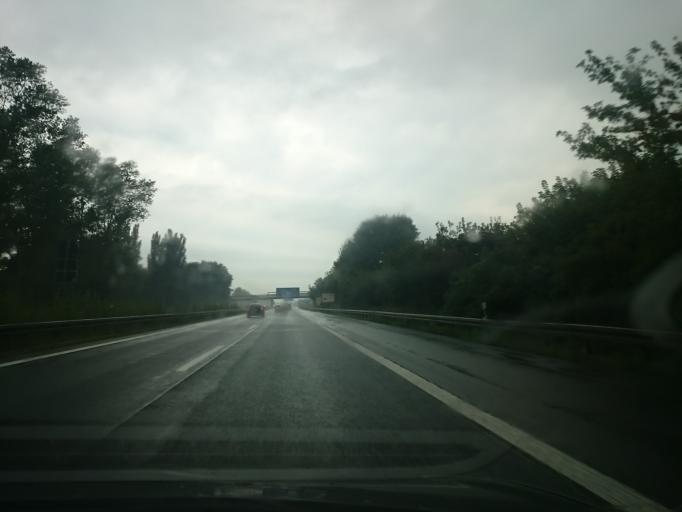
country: DE
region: Brandenburg
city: Kremmen
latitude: 52.7062
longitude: 13.0520
